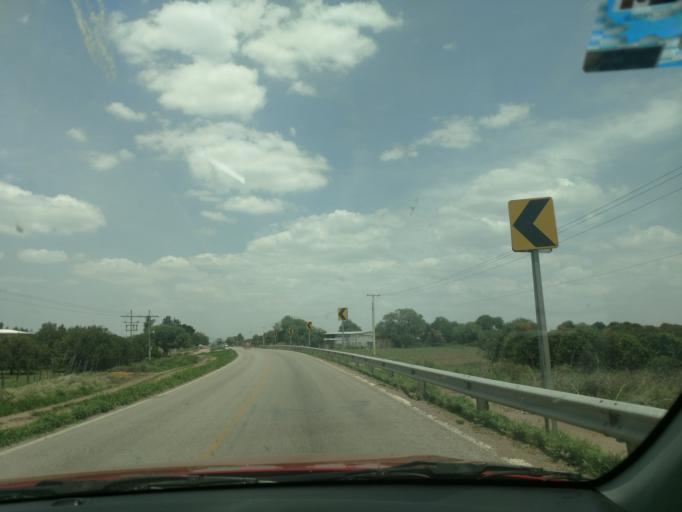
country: MX
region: San Luis Potosi
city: Ciudad Fernandez
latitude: 21.9507
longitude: -100.0640
